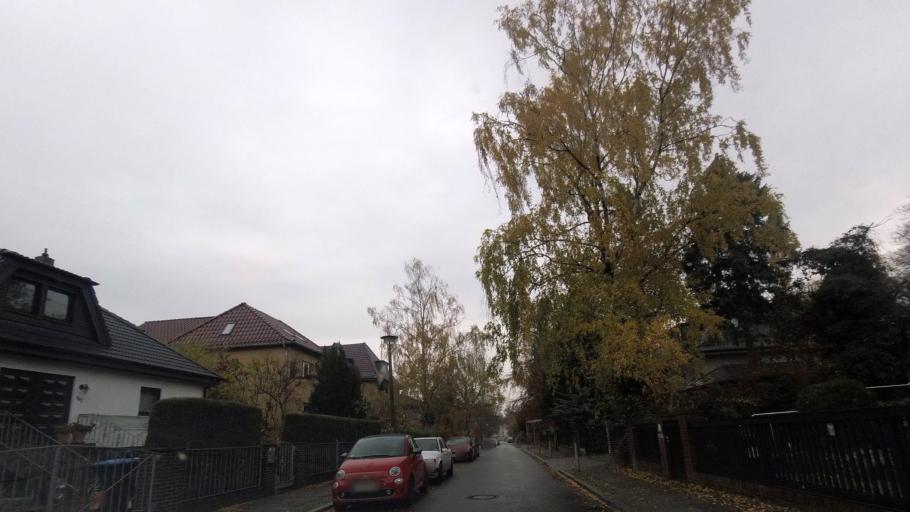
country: DE
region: Berlin
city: Weissensee
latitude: 52.5591
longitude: 13.4555
